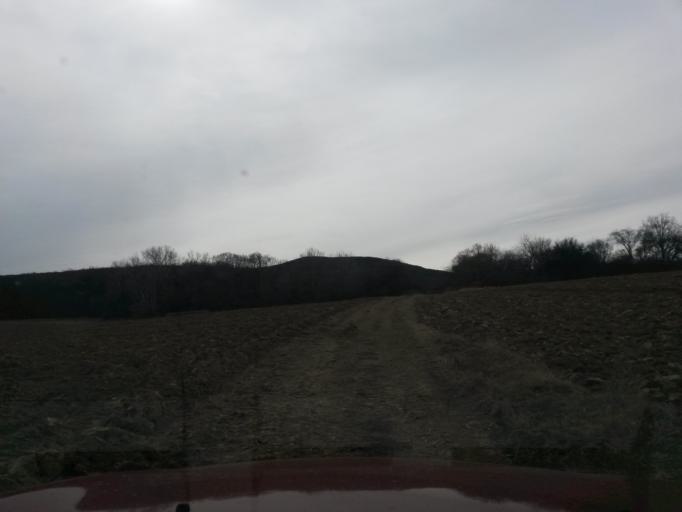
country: HU
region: Borsod-Abauj-Zemplen
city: Gonc
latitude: 48.5805
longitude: 21.3765
